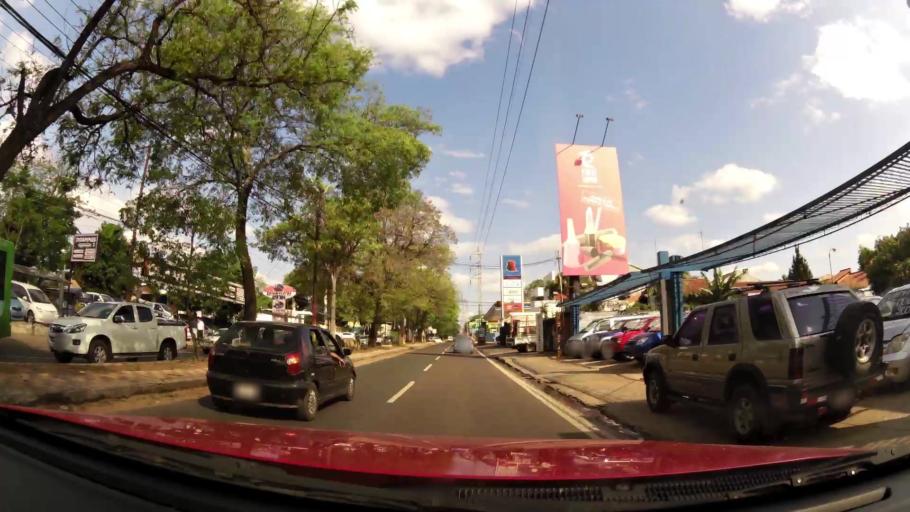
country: PY
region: Central
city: Fernando de la Mora
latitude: -25.3133
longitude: -57.5290
